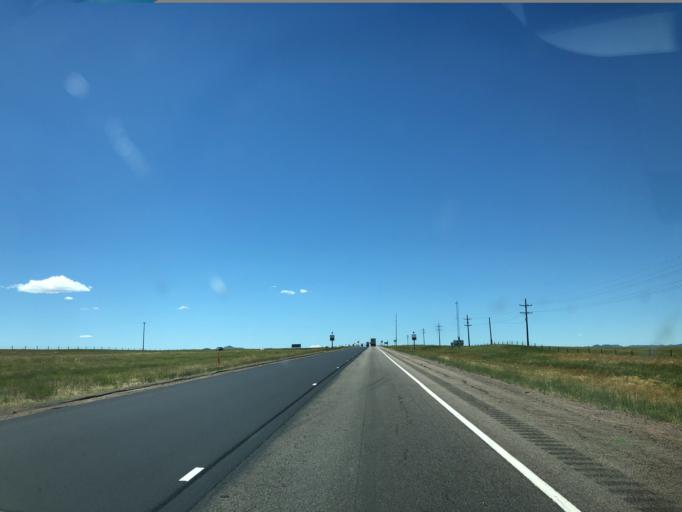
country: US
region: Wyoming
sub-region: Laramie County
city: Cheyenne
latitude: 41.1003
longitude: -105.0722
